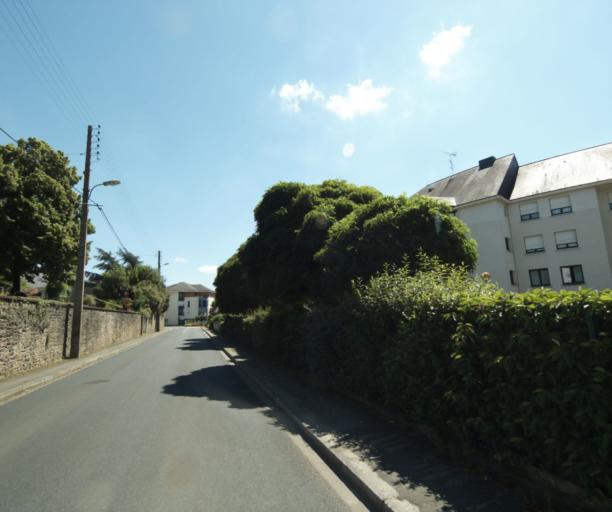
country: FR
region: Pays de la Loire
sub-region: Departement de la Mayenne
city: Laval
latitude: 48.0816
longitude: -0.7698
